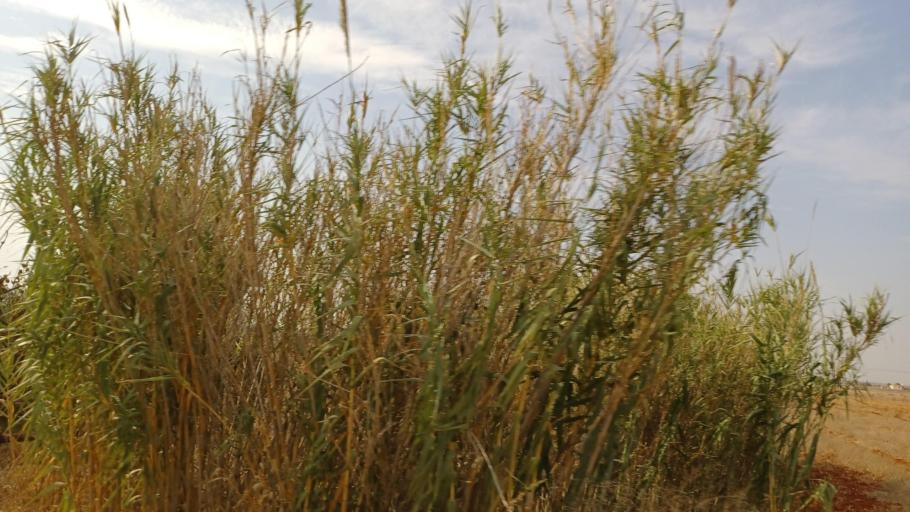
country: CY
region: Ammochostos
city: Frenaros
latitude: 35.0613
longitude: 33.8883
